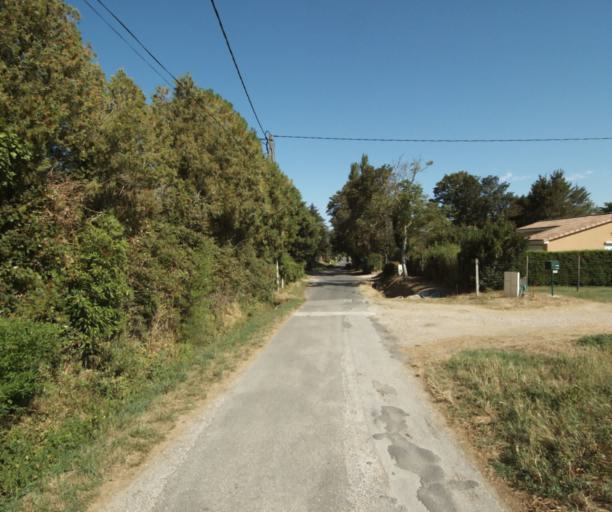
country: FR
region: Midi-Pyrenees
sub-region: Departement de la Haute-Garonne
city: Revel
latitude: 43.4502
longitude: 2.0190
